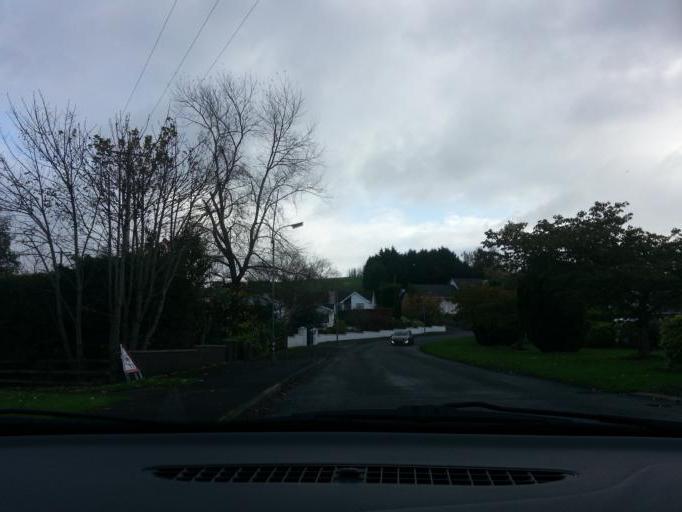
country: GB
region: Northern Ireland
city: Lisnaskea
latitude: 54.2440
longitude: -7.4352
